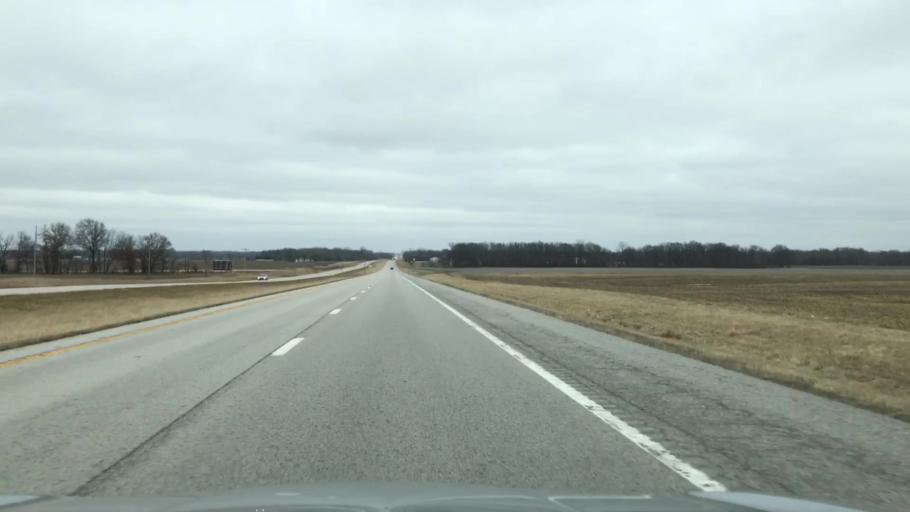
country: US
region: Missouri
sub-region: Livingston County
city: Chillicothe
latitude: 39.7764
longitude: -93.4572
